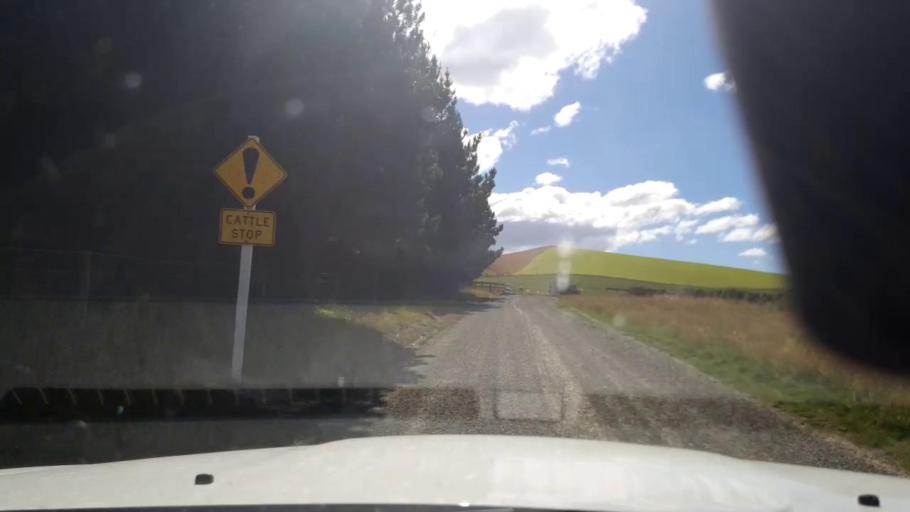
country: NZ
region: Canterbury
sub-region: Timaru District
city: Pleasant Point
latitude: -44.3200
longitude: 170.8769
